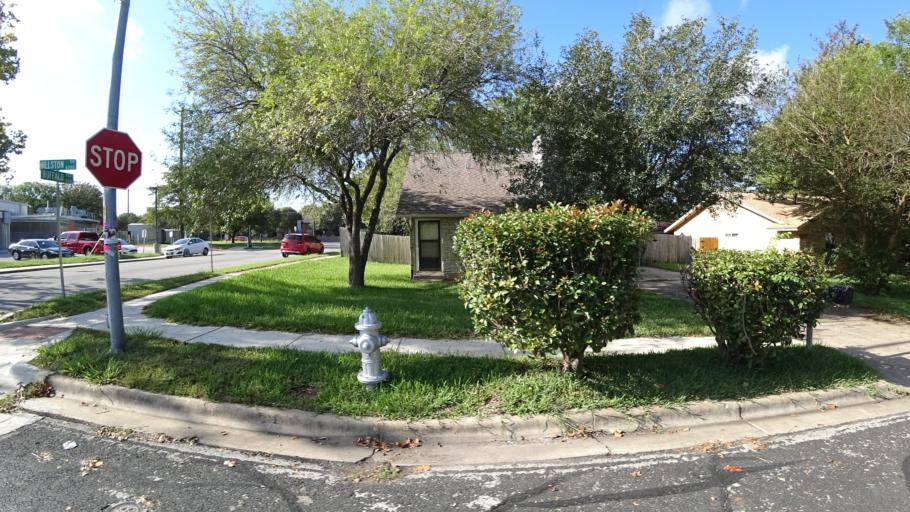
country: US
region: Texas
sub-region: Travis County
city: Rollingwood
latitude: 30.2107
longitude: -97.8070
